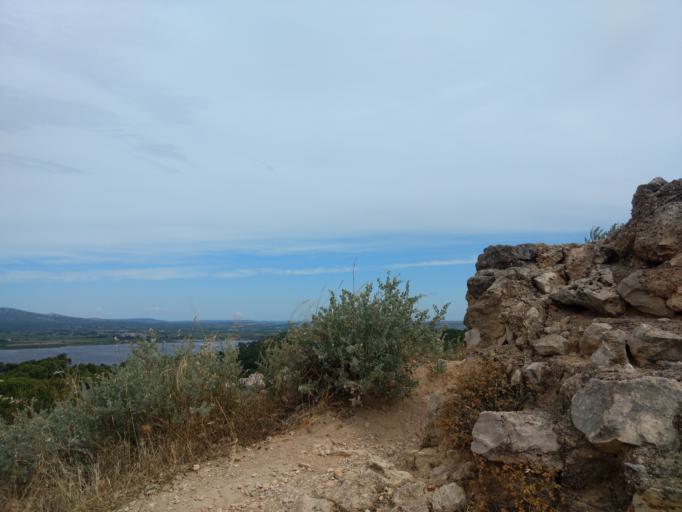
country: FR
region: Languedoc-Roussillon
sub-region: Departement de l'Aude
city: Leucate
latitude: 42.9085
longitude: 3.0251
